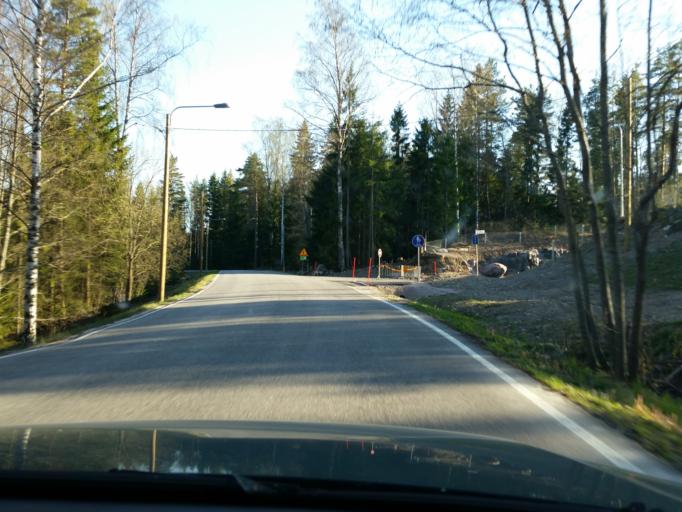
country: FI
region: Uusimaa
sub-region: Helsinki
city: Kirkkonummi
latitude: 60.1273
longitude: 24.5171
